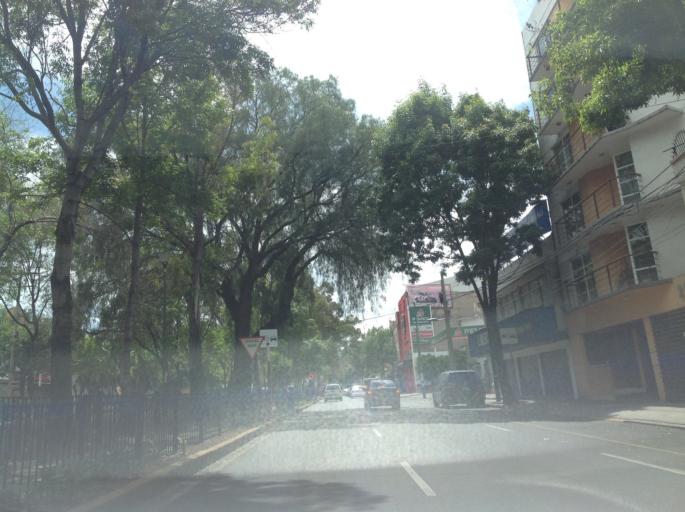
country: MX
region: Mexico City
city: Miguel Hidalgo
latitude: 19.4544
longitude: -99.1972
